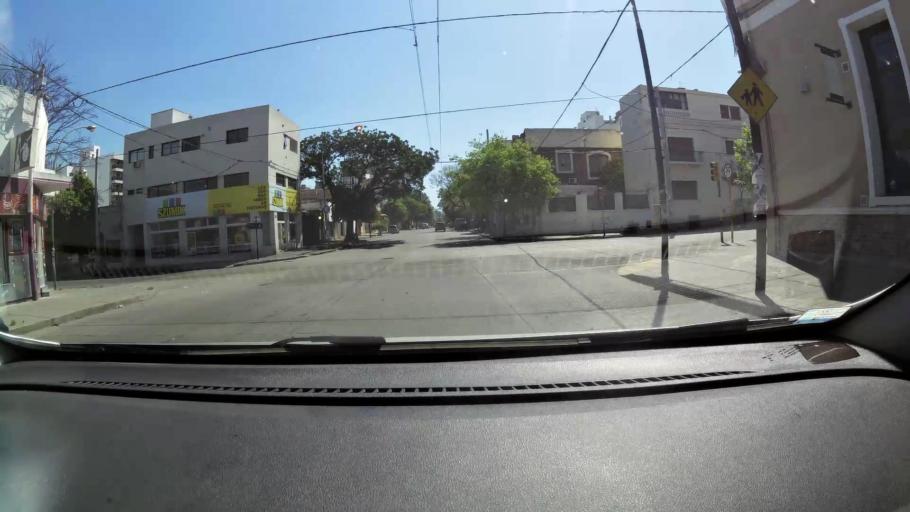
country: AR
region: Cordoba
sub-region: Departamento de Capital
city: Cordoba
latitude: -31.4112
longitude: -64.1695
